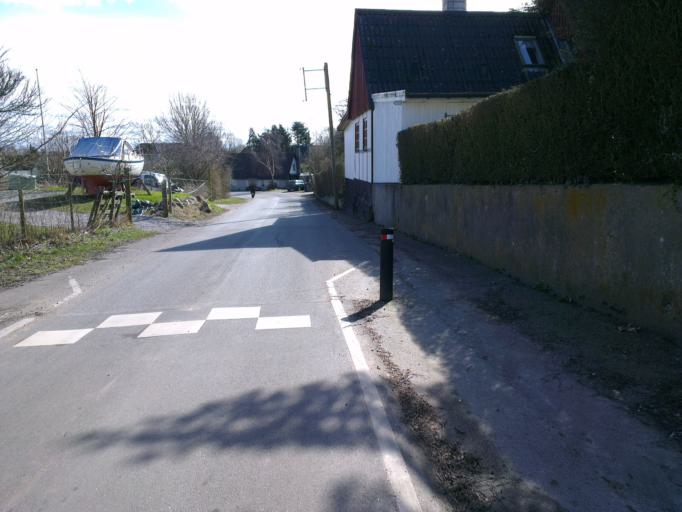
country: DK
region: Capital Region
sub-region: Frederikssund Kommune
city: Skibby
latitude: 55.7357
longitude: 12.0317
